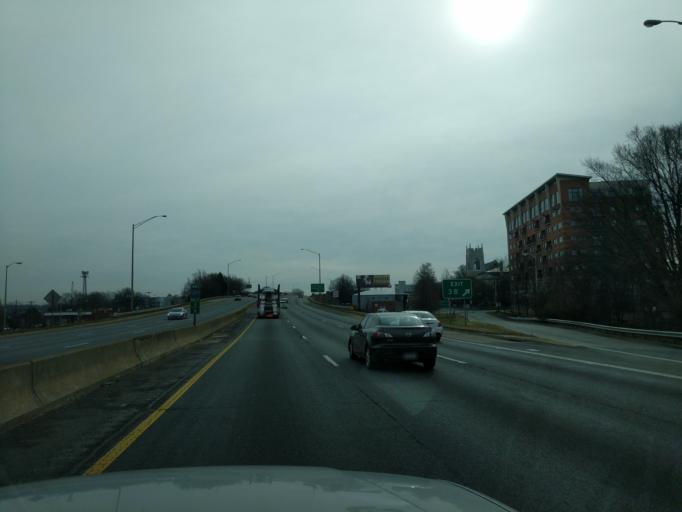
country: US
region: North Carolina
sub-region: Mecklenburg County
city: Charlotte
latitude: 35.2348
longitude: -80.8377
